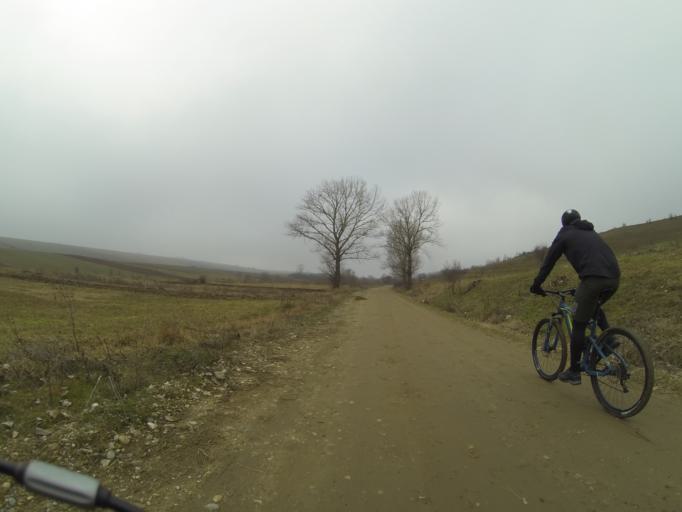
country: RO
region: Mehedinti
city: Padina Mica
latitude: 44.4880
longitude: 23.0163
